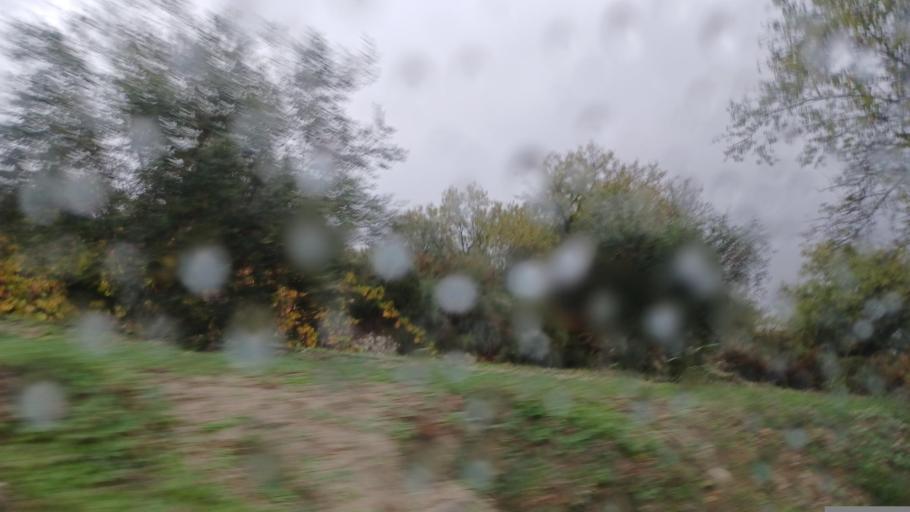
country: CY
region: Pafos
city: Mesogi
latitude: 34.8644
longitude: 32.5419
